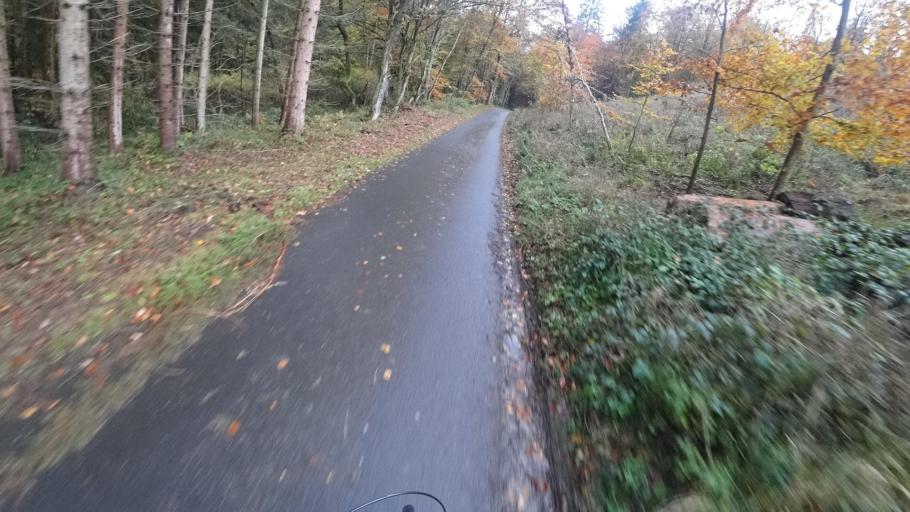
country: DE
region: Rheinland-Pfalz
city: Ney
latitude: 50.1687
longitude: 7.5223
